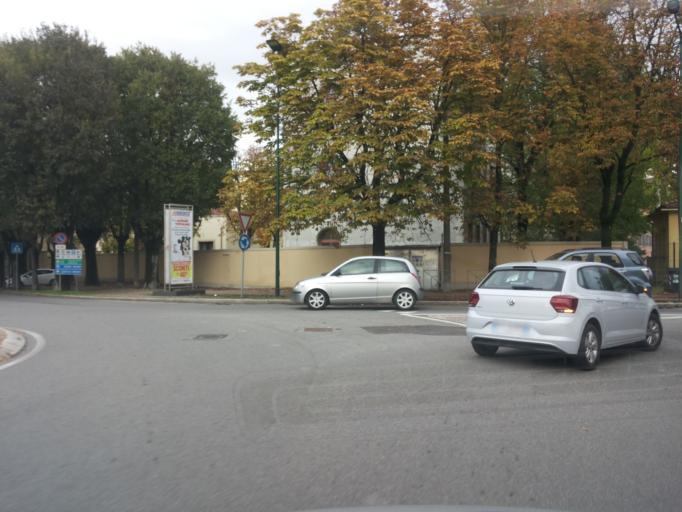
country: IT
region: Piedmont
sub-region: Provincia di Alessandria
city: Casale Monferrato
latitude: 45.1351
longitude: 8.4459
